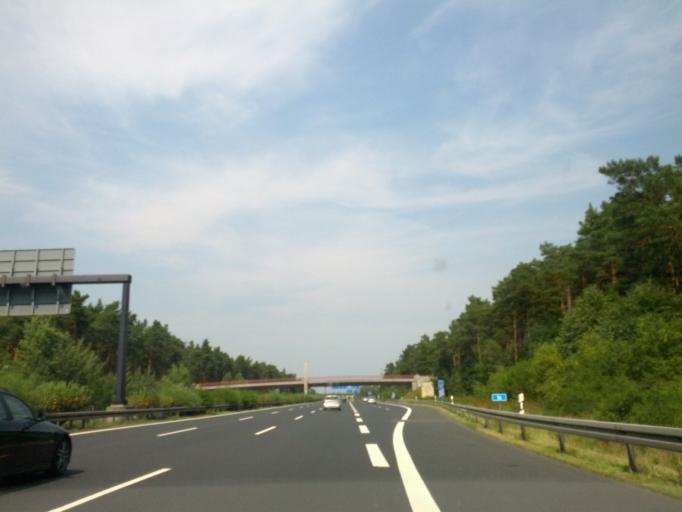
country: DE
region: Brandenburg
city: Fichtenwalde
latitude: 52.2765
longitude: 12.9118
